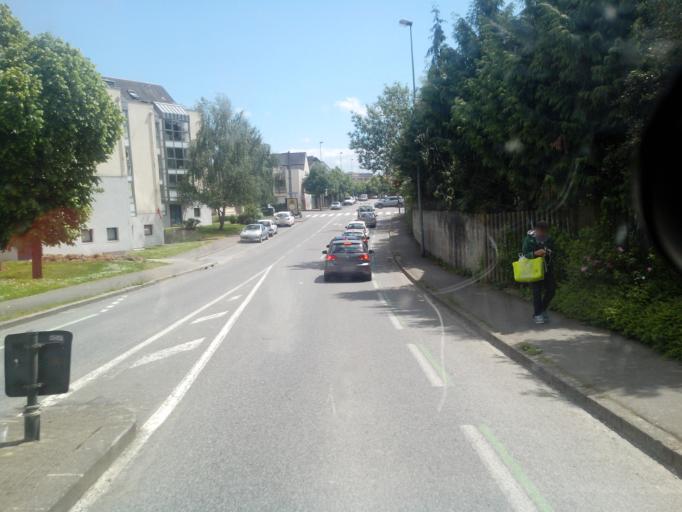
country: FR
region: Brittany
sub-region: Departement d'Ille-et-Vilaine
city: Rennes
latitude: 48.0971
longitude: -1.6933
